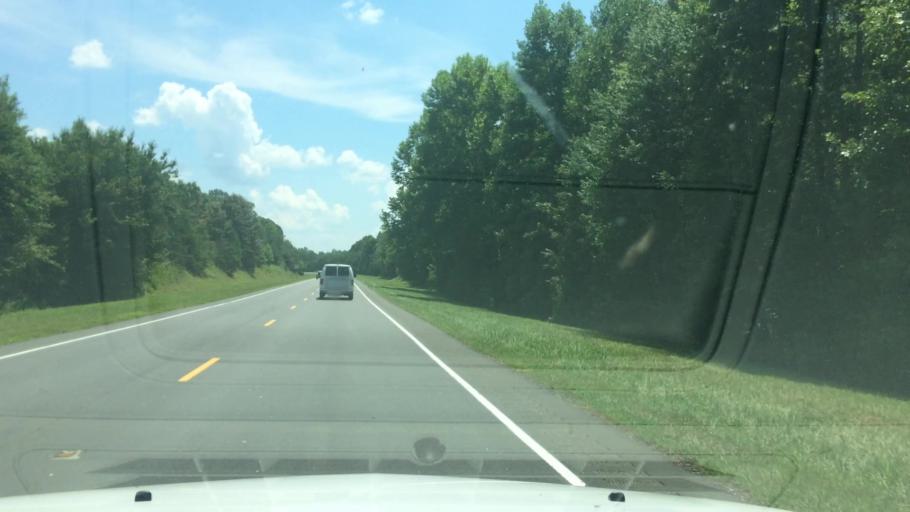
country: US
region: North Carolina
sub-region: Alexander County
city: Stony Point
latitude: 35.8298
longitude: -81.0151
